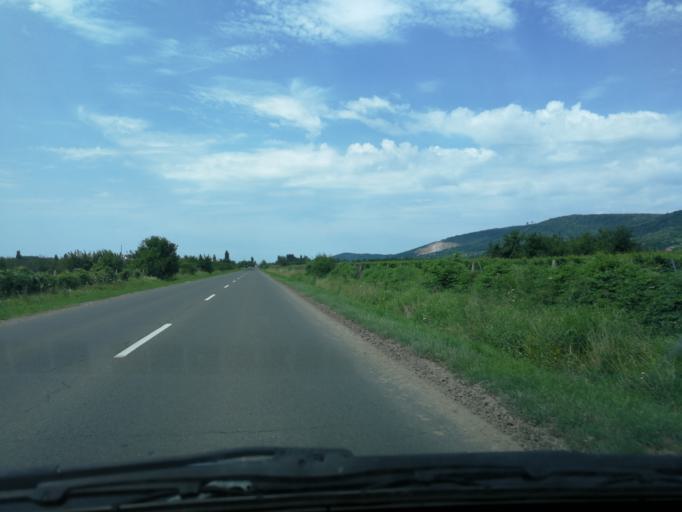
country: HU
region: Baranya
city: Siklos
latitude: 45.8671
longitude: 18.2932
